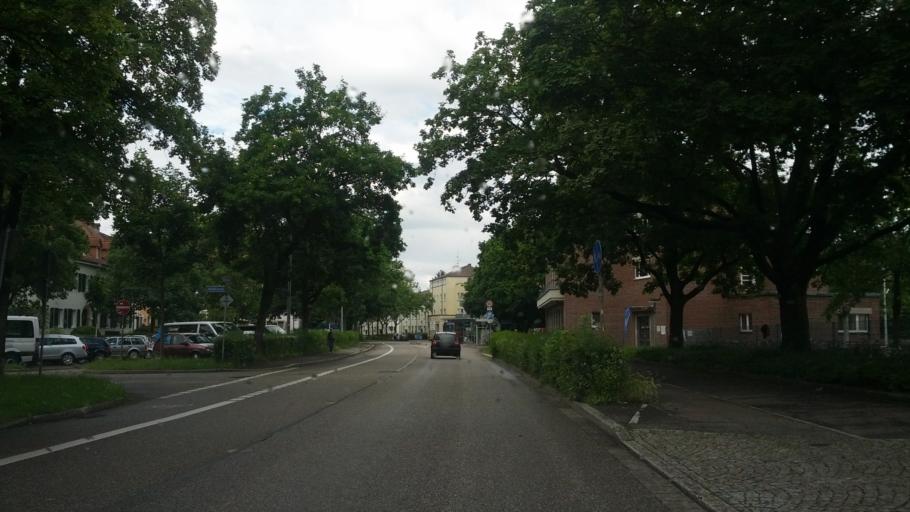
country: DE
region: Baden-Wuerttemberg
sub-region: Freiburg Region
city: Freiburg
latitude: 47.9890
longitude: 7.8824
